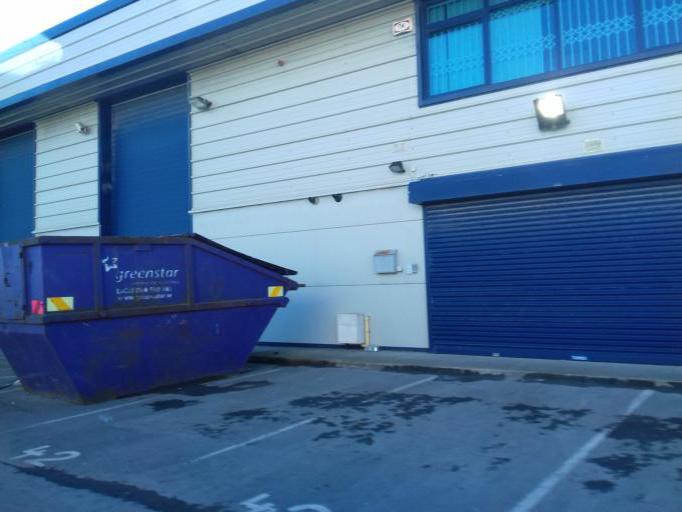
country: IE
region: Leinster
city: Castleknock
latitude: 53.4062
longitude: -6.3420
